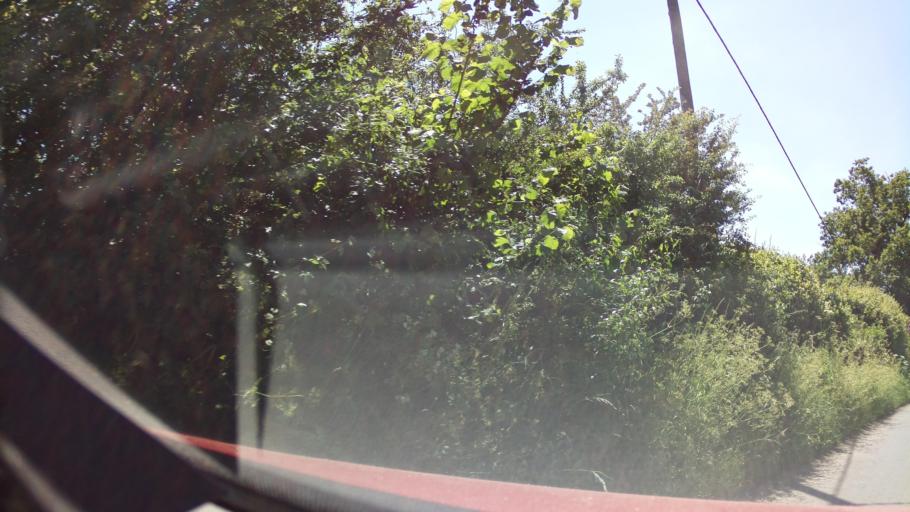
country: GB
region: England
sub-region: Wiltshire
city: Bremhill
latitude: 51.4710
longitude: -2.0688
